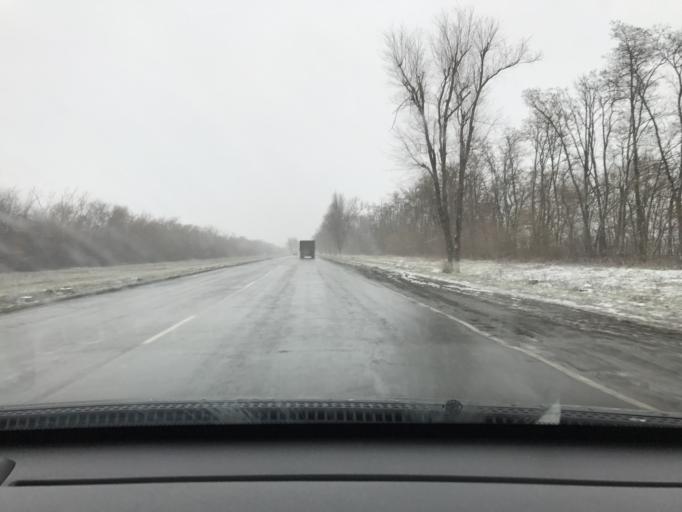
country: RU
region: Rostov
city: Yegorlykskaya
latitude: 46.5964
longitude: 40.6226
